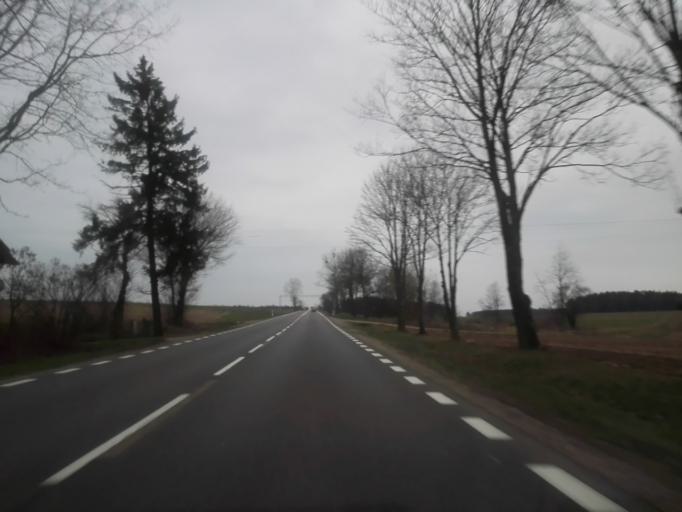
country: PL
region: Podlasie
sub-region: Powiat kolnenski
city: Stawiski
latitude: 53.4542
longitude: 22.1901
